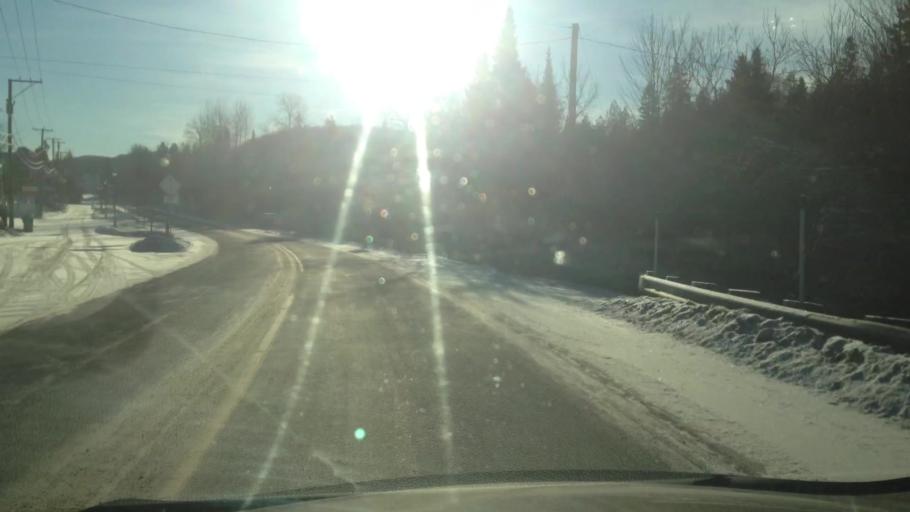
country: CA
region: Quebec
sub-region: Laurentides
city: Mont-Tremblant
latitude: 45.9456
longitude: -74.5499
